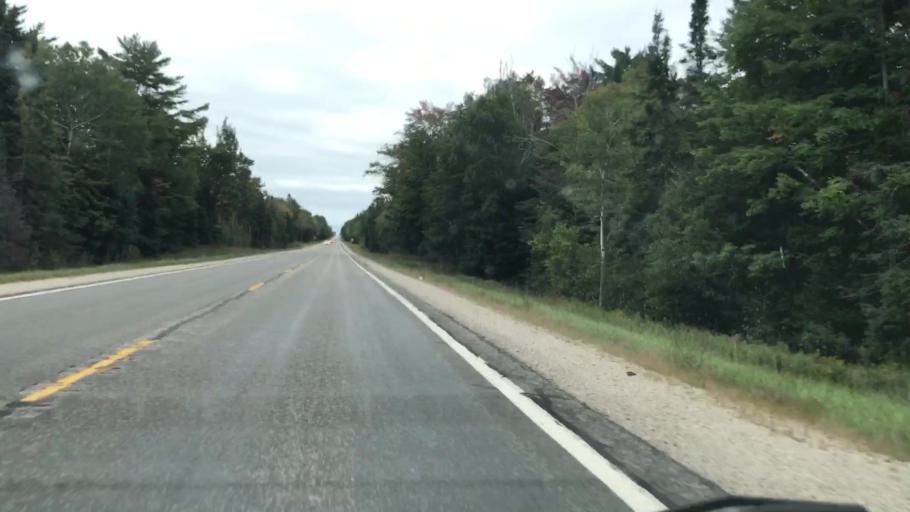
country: US
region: Michigan
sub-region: Luce County
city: Newberry
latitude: 46.2351
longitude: -85.5722
